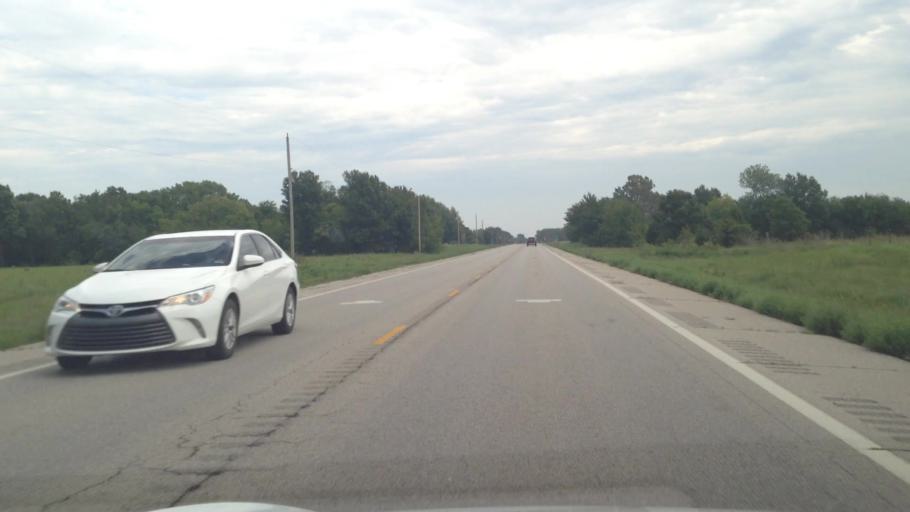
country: US
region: Kansas
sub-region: Crawford County
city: Pittsburg
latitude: 37.3391
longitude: -94.7826
